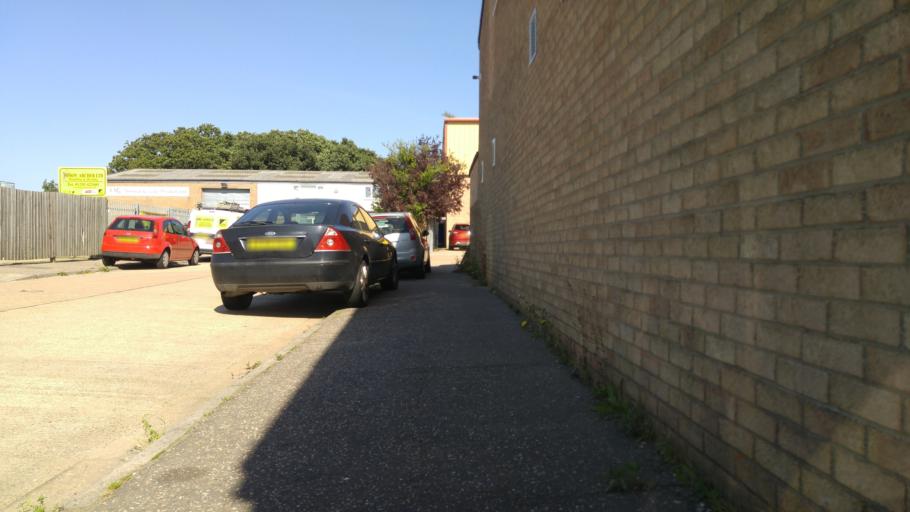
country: GB
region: England
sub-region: Essex
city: Clacton-on-Sea
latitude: 51.8171
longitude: 1.1741
